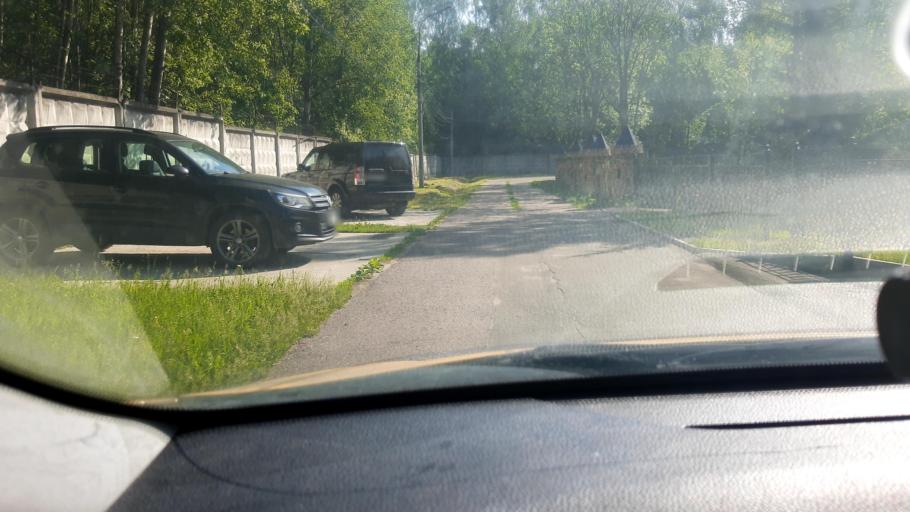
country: RU
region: Moskovskaya
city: Lyubuchany
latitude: 55.3141
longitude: 37.6255
